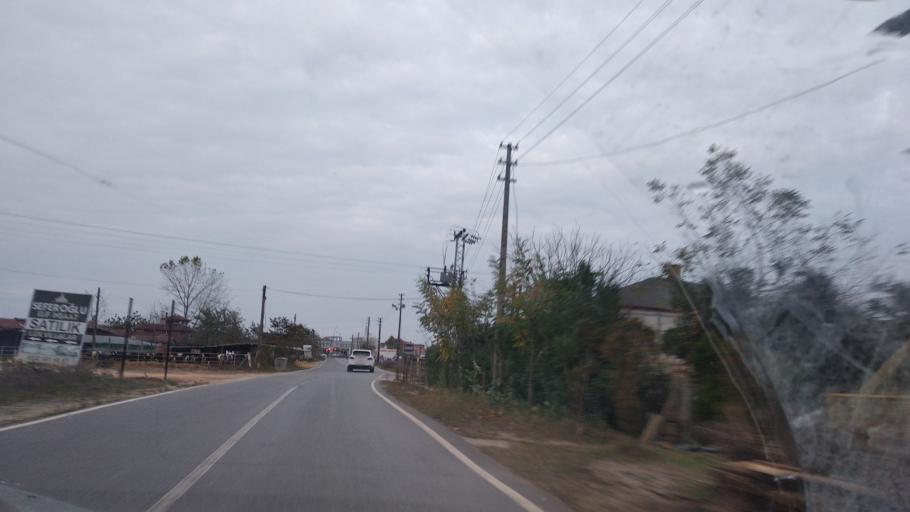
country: TR
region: Sakarya
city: Karasu
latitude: 41.0845
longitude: 30.7391
